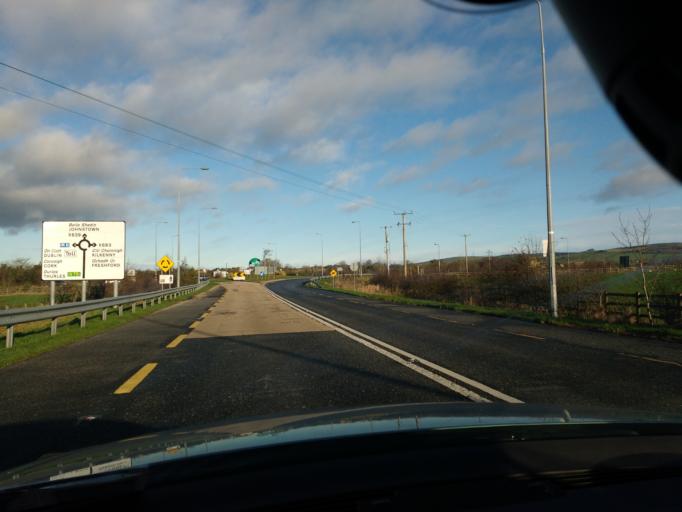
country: IE
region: Leinster
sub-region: Laois
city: Rathdowney
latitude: 52.7265
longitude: -7.5743
